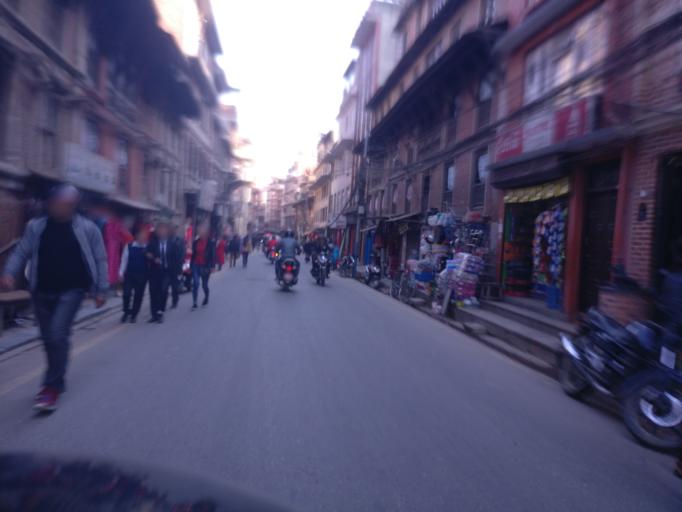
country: NP
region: Central Region
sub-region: Bagmati Zone
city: Patan
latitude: 27.6753
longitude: 85.3192
